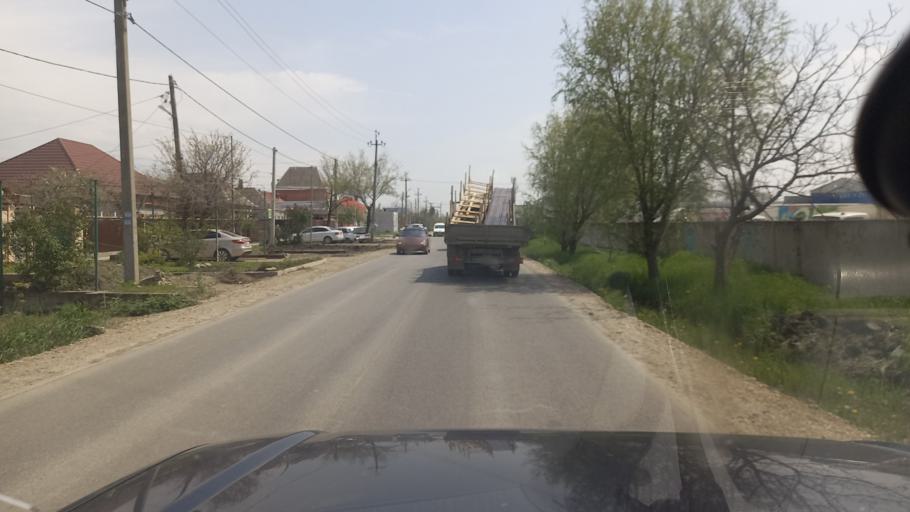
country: RU
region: Adygeya
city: Yablonovskiy
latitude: 44.9885
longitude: 38.9561
